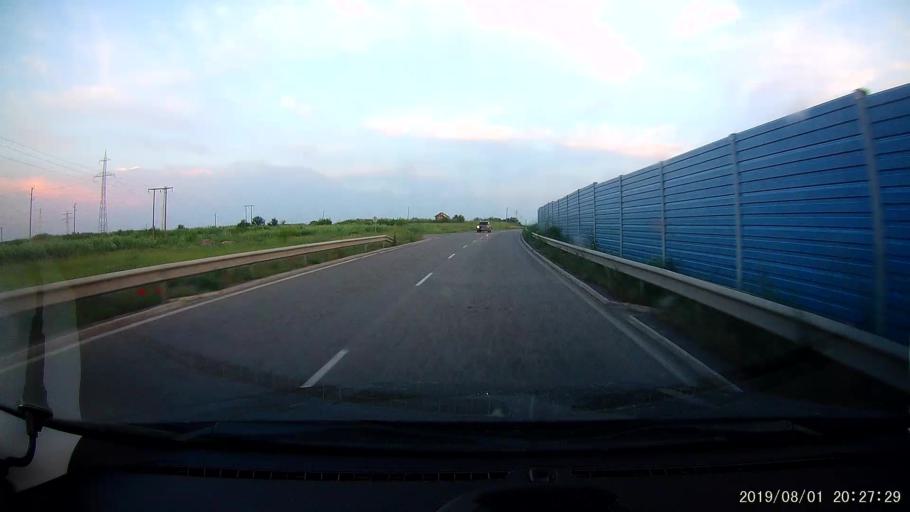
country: BG
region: Yambol
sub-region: Obshtina Elkhovo
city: Elkhovo
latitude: 42.1797
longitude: 26.5845
